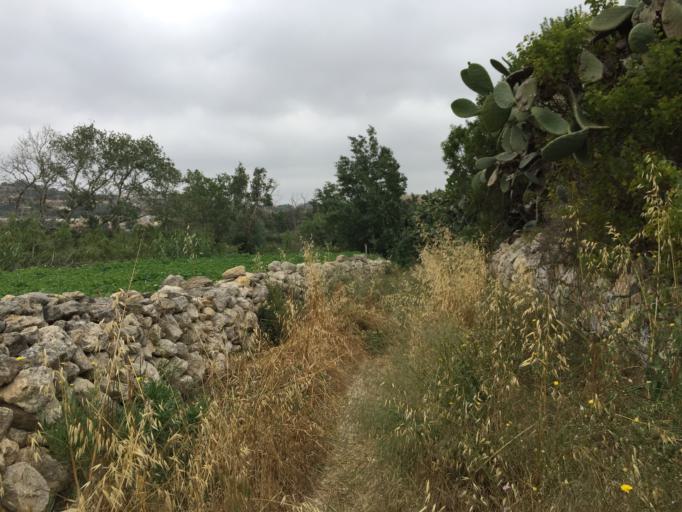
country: MT
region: Ir-Rabat
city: Rabat
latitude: 35.8870
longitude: 14.3804
